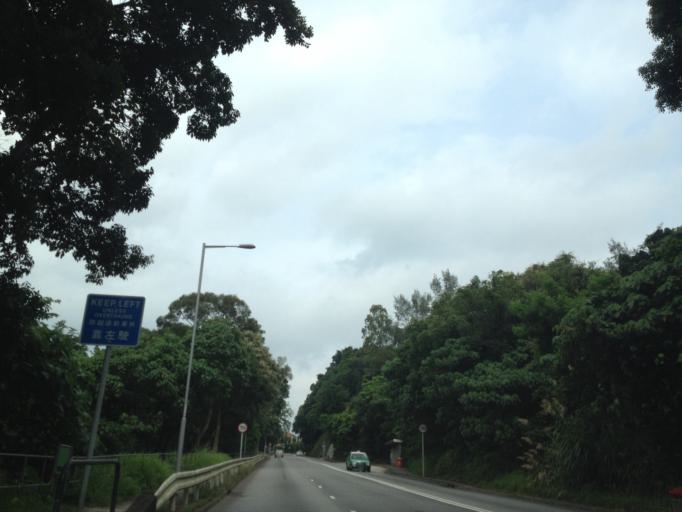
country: HK
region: Tai Po
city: Tai Po
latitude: 22.4410
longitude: 114.1809
